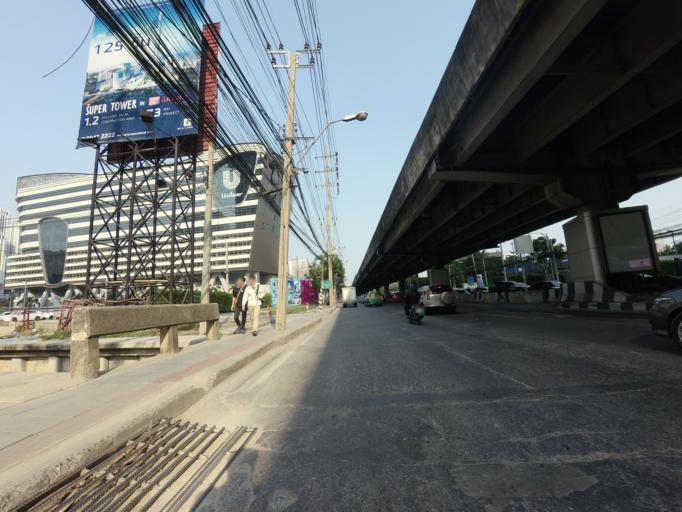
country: TH
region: Bangkok
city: Din Daeng
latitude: 13.7561
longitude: 100.5663
